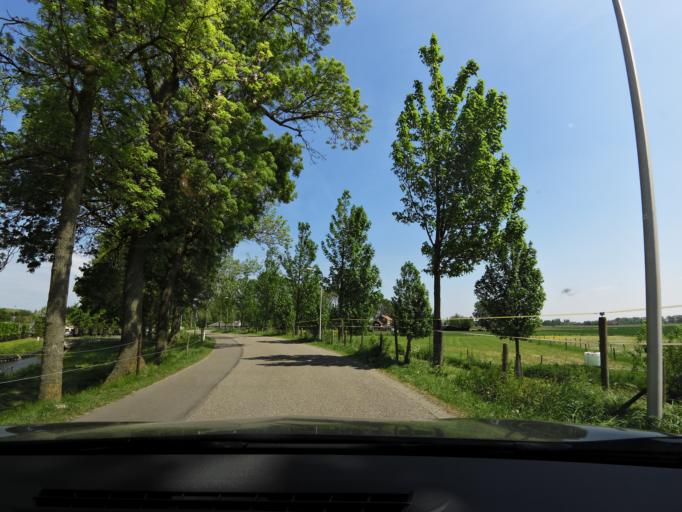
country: NL
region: South Holland
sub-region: Gemeente Albrandswaard
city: Rhoon
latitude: 51.8557
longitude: 4.4375
